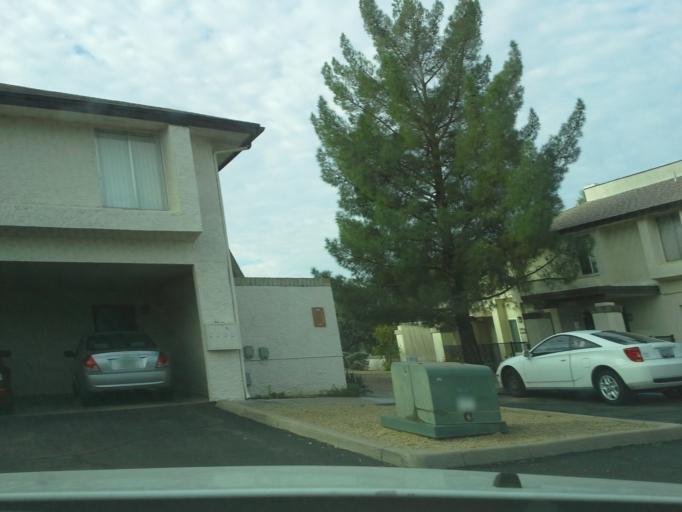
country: US
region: Arizona
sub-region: Maricopa County
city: Glendale
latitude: 33.6099
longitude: -112.0624
